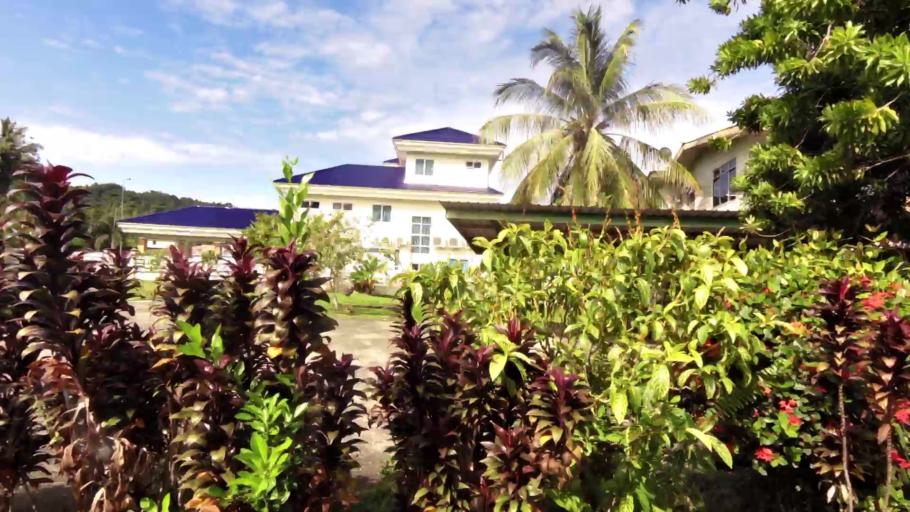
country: BN
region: Brunei and Muara
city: Bandar Seri Begawan
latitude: 4.9022
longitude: 114.9752
